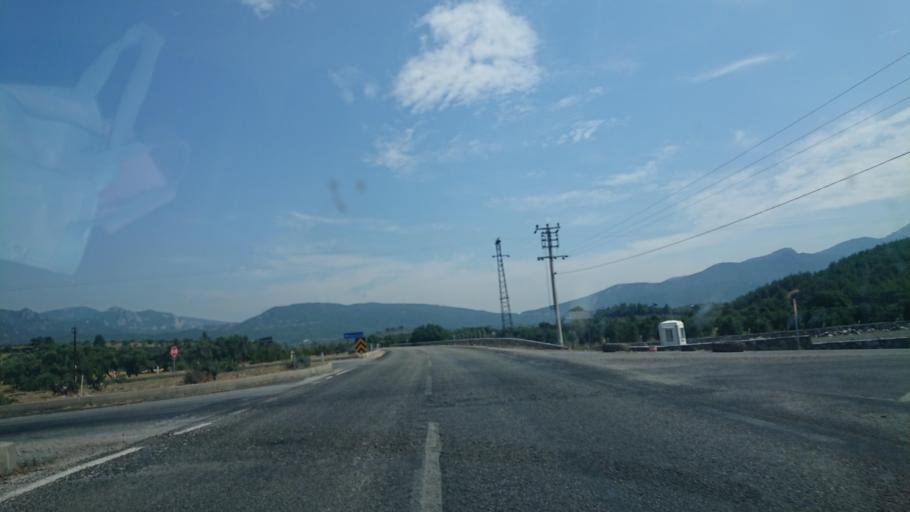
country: TR
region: Izmir
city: Dagkizilca
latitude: 38.3080
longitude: 27.4109
